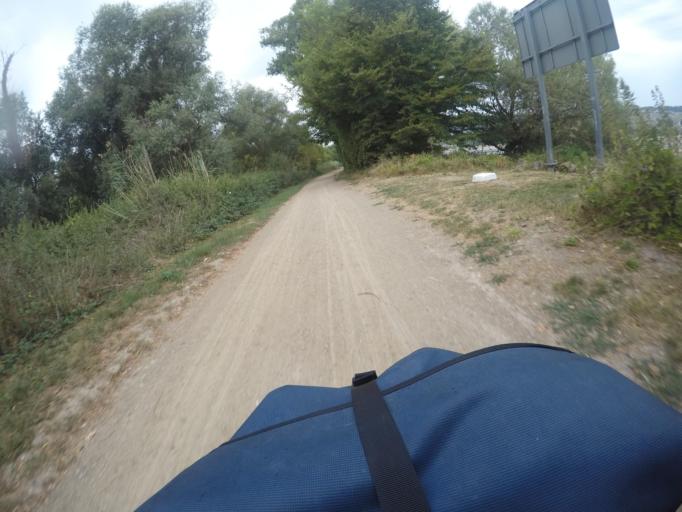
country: DE
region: Hesse
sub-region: Regierungsbezirk Darmstadt
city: Rudesheim am Rhein
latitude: 49.9705
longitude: 7.9478
